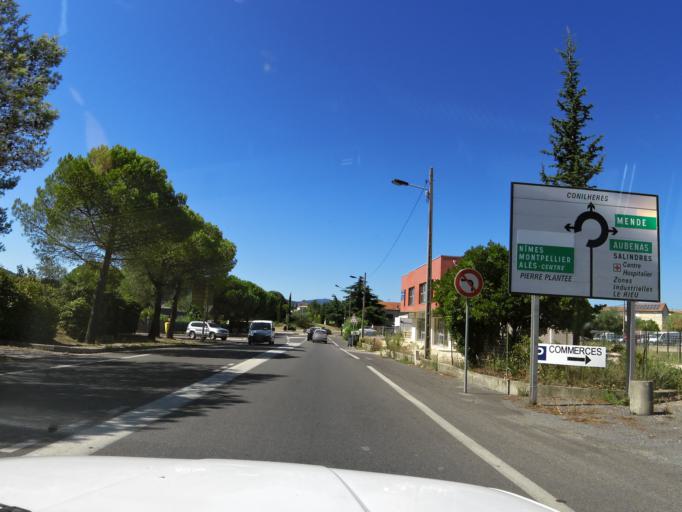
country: FR
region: Languedoc-Roussillon
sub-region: Departement du Gard
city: Ales
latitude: 44.1120
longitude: 4.1079
